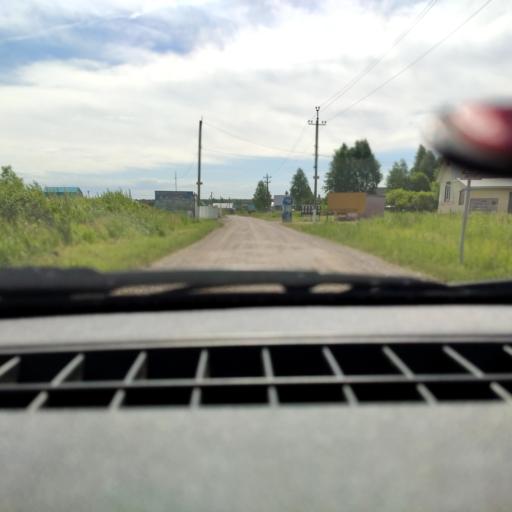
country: RU
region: Bashkortostan
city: Kabakovo
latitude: 54.7270
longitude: 56.2060
